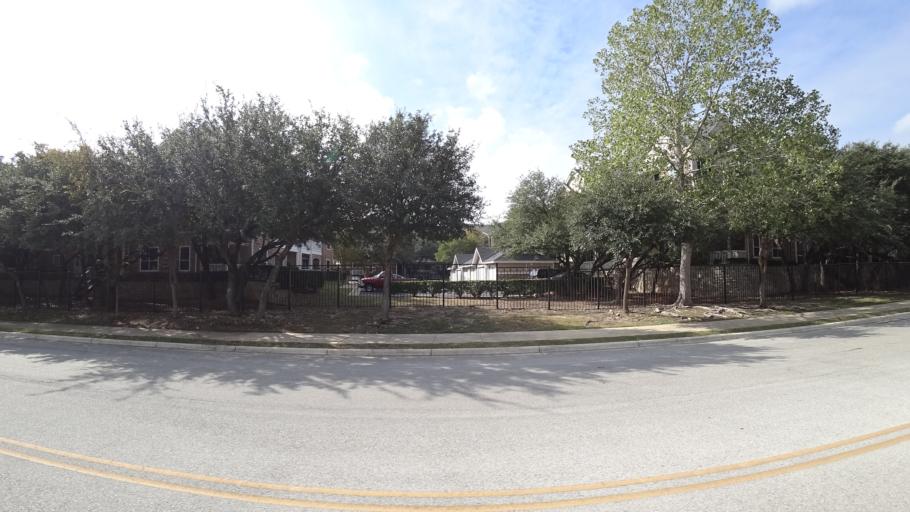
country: US
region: Texas
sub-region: Williamson County
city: Jollyville
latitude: 30.4379
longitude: -97.7331
